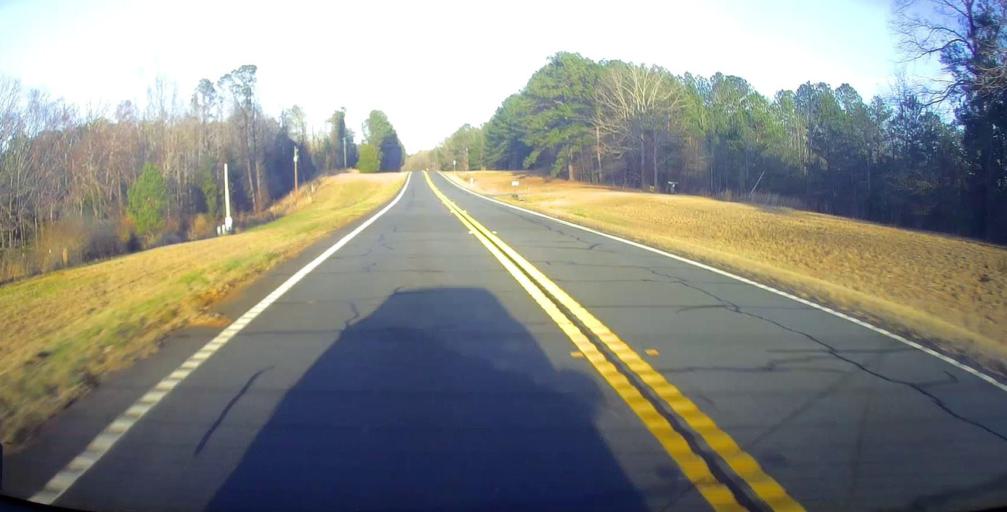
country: US
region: Georgia
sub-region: Talbot County
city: Talbotton
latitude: 32.7879
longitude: -84.5144
